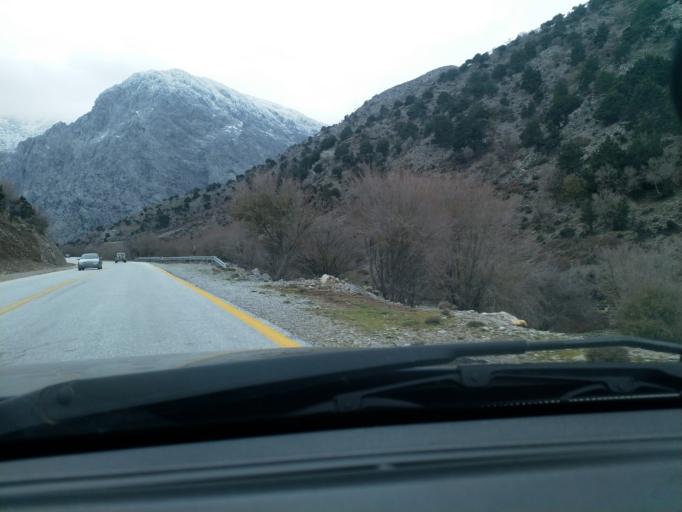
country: GR
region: Crete
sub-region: Nomos Chanias
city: Perivolia
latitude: 35.3137
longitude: 23.9156
